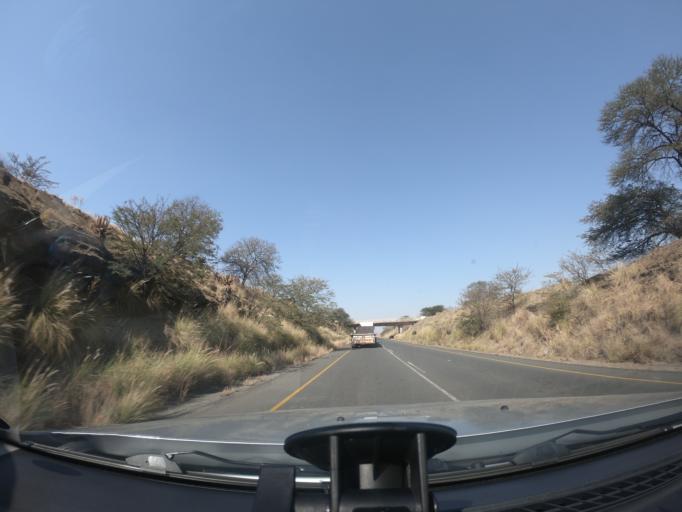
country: ZA
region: KwaZulu-Natal
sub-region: uThukela District Municipality
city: Ladysmith
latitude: -28.7496
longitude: 29.8218
